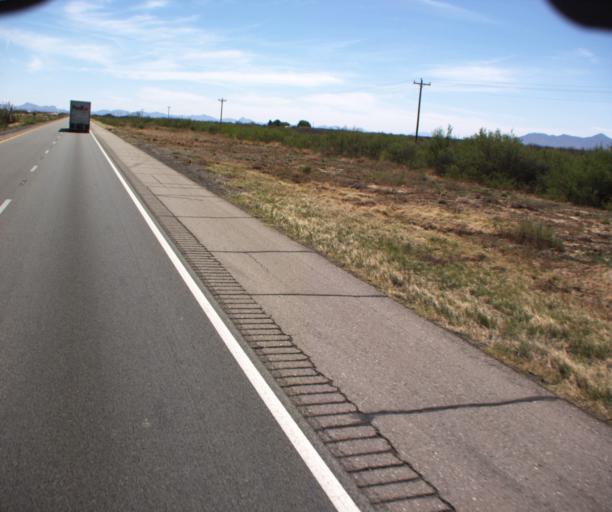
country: US
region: Arizona
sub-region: Cochise County
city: Willcox
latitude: 32.3098
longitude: -109.4094
